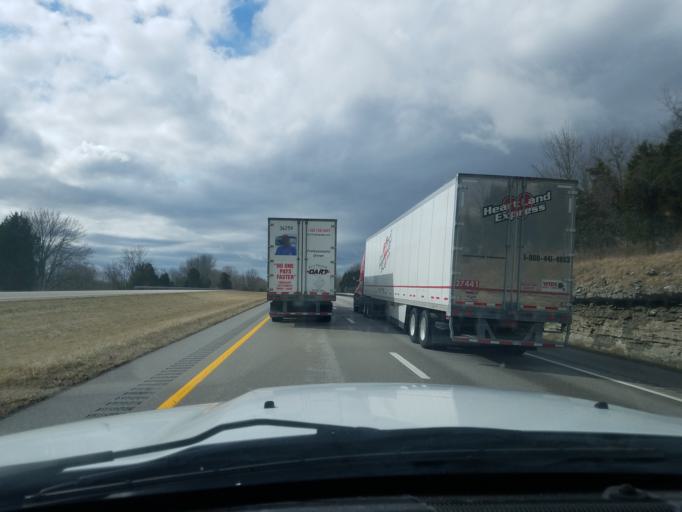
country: US
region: Kentucky
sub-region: Montgomery County
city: Mount Sterling
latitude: 38.0941
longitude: -83.8705
